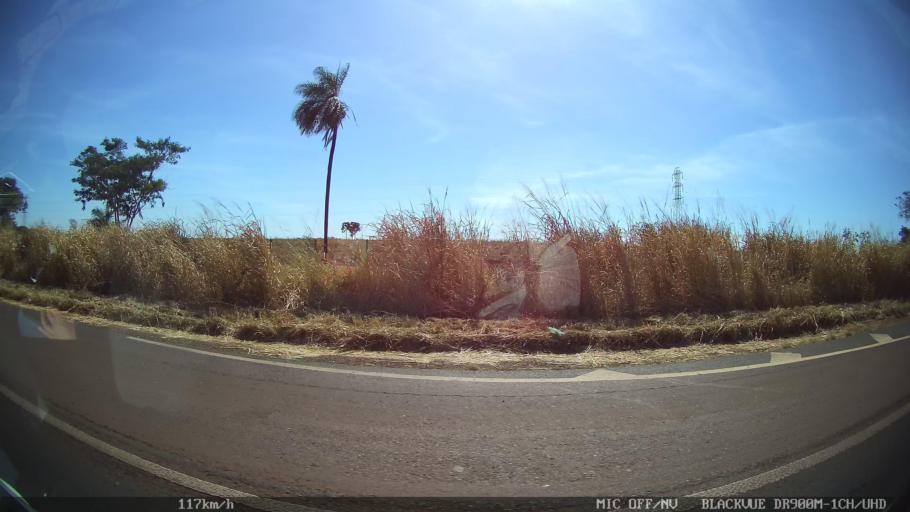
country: BR
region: Sao Paulo
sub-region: Barretos
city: Barretos
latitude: -20.4948
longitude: -48.5300
